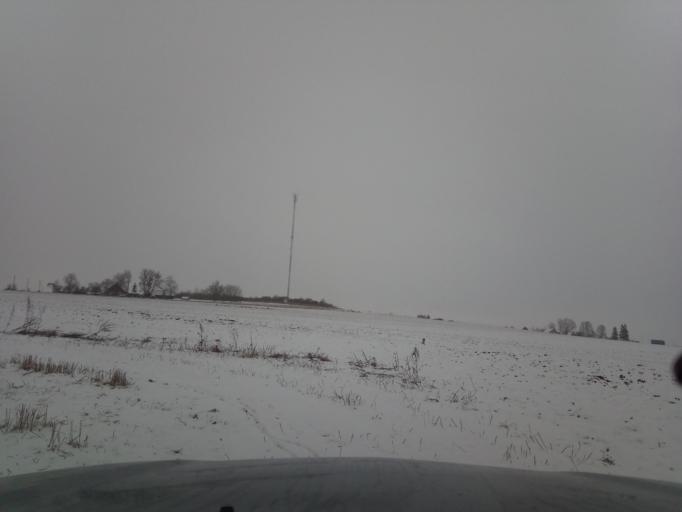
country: LT
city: Ramygala
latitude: 55.4851
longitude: 24.2934
